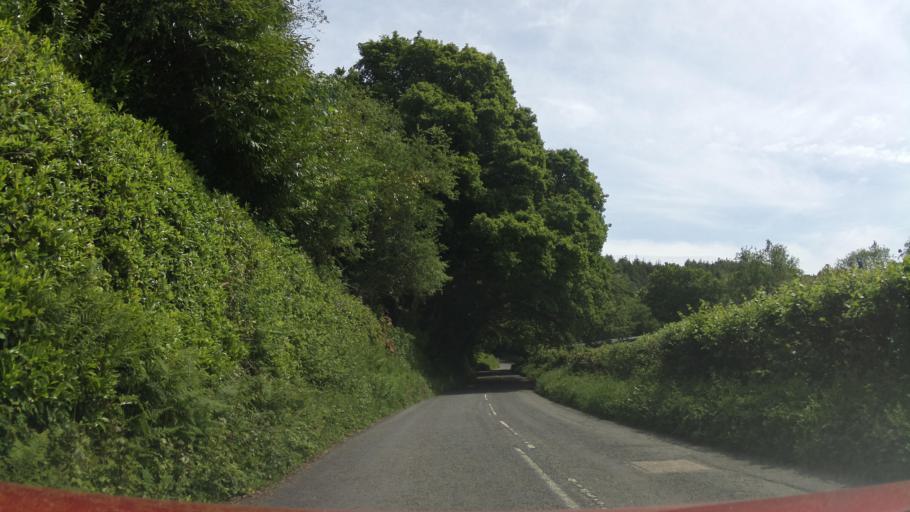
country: GB
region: England
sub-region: Devon
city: South Brent
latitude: 50.3658
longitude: -3.7855
